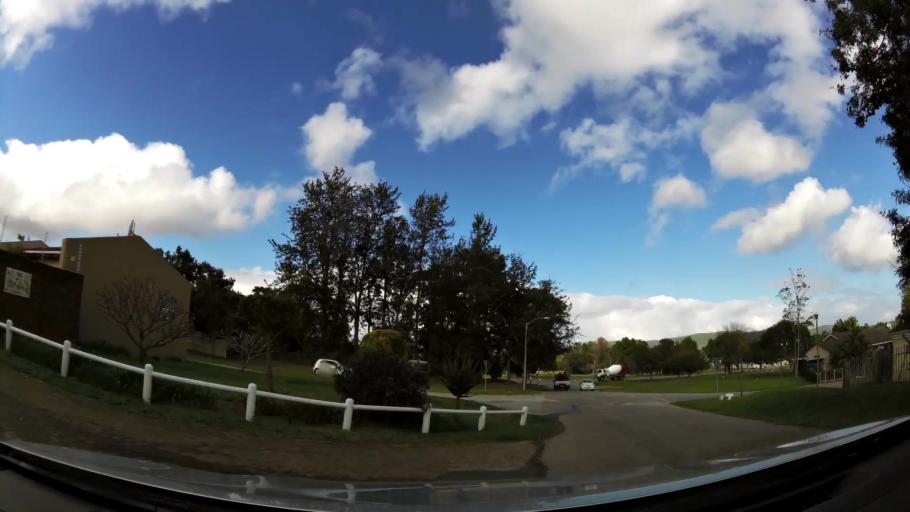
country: ZA
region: Western Cape
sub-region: Eden District Municipality
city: Knysna
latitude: -34.0397
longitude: 23.0722
